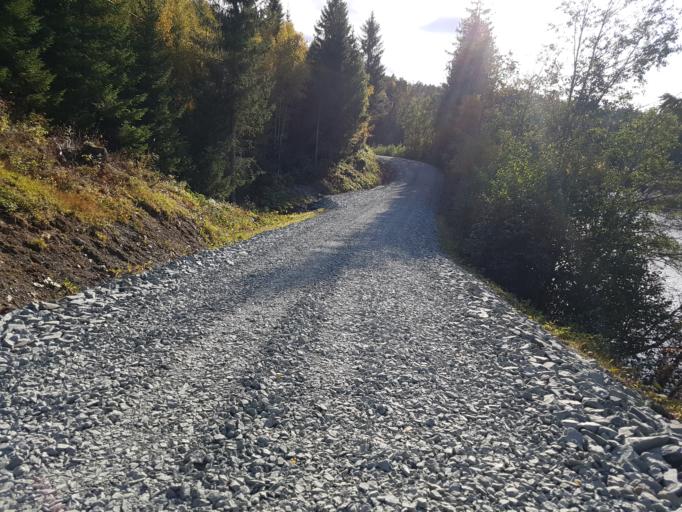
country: NO
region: Sor-Trondelag
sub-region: Klaebu
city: Klaebu
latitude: 63.3428
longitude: 10.5850
